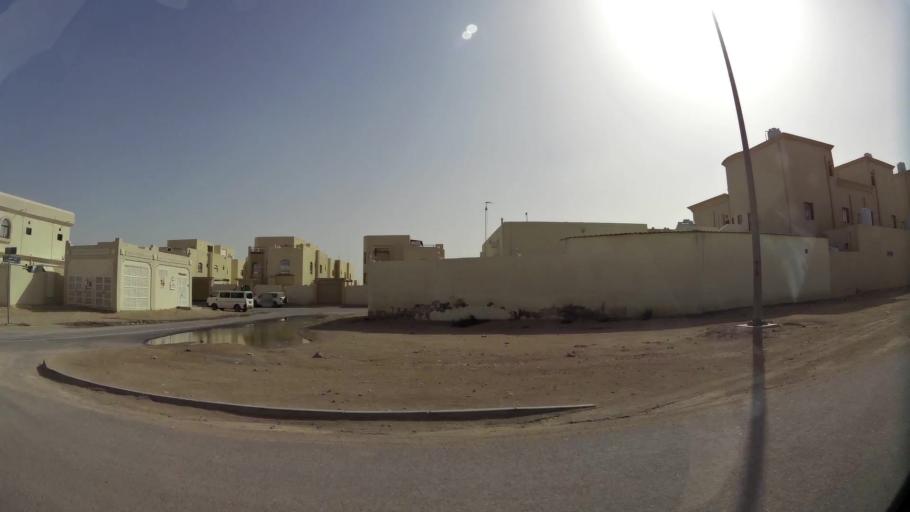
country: QA
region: Baladiyat ar Rayyan
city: Ar Rayyan
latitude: 25.3417
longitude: 51.4207
